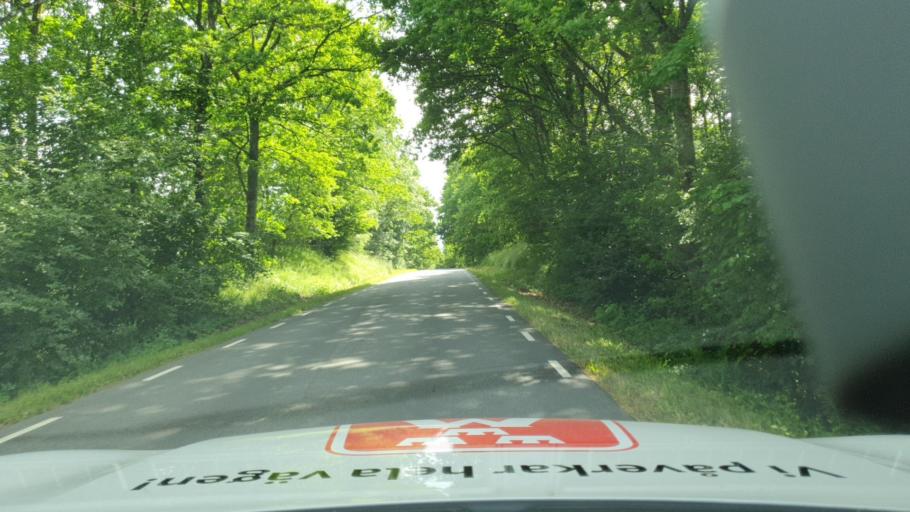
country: SE
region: Skane
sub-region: Tomelilla Kommun
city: Tomelilla
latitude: 55.6884
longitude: 13.9460
